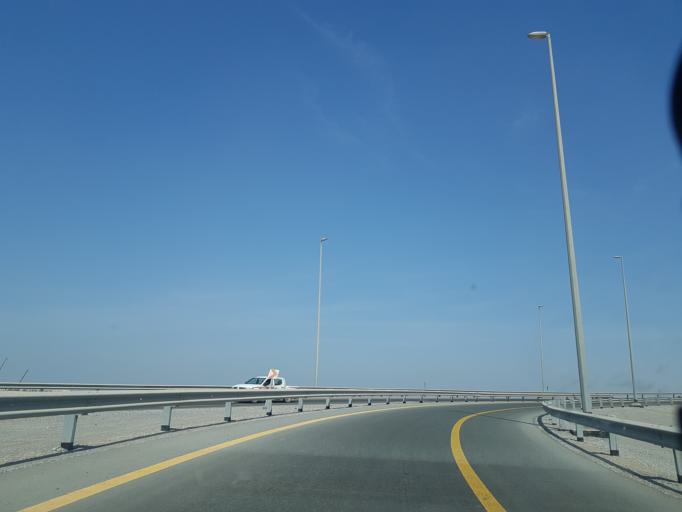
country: AE
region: Ra's al Khaymah
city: Ras al-Khaimah
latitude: 25.6713
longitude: 55.8789
